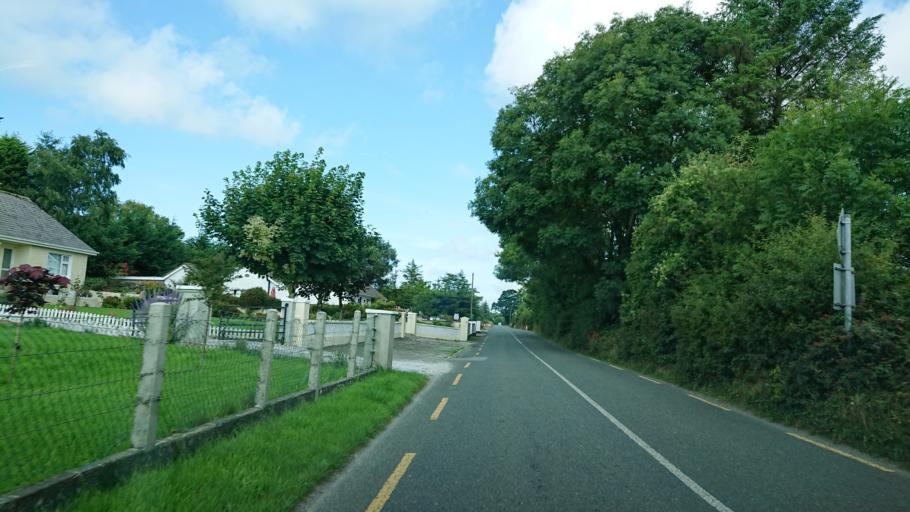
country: IE
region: Munster
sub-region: Ciarrai
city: Cill Airne
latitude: 52.0861
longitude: -9.5279
